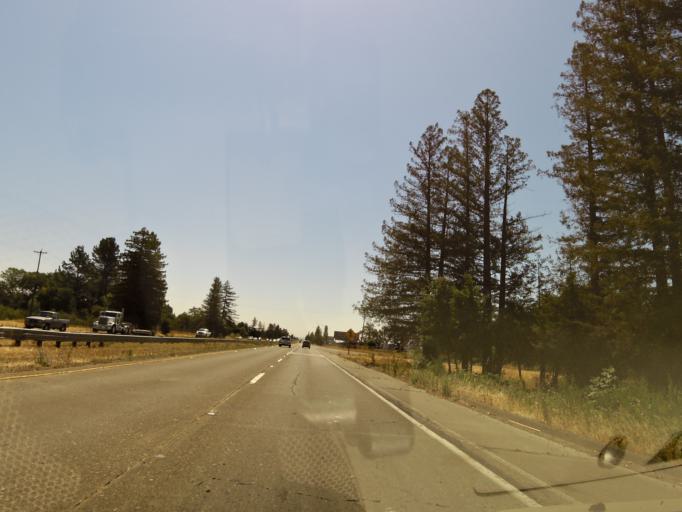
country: US
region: California
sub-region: Sonoma County
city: Windsor
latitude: 38.5668
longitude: -122.8279
